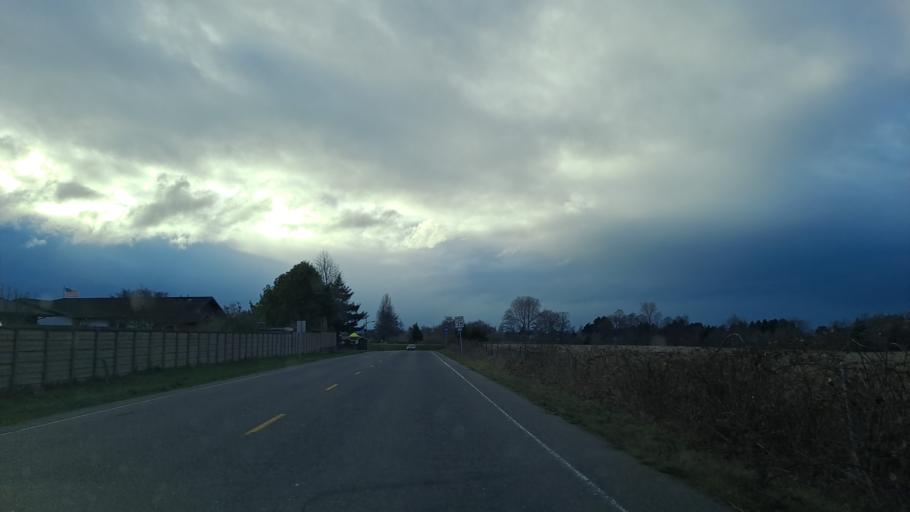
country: US
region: California
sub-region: Humboldt County
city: Fortuna
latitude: 40.5831
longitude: -124.1343
